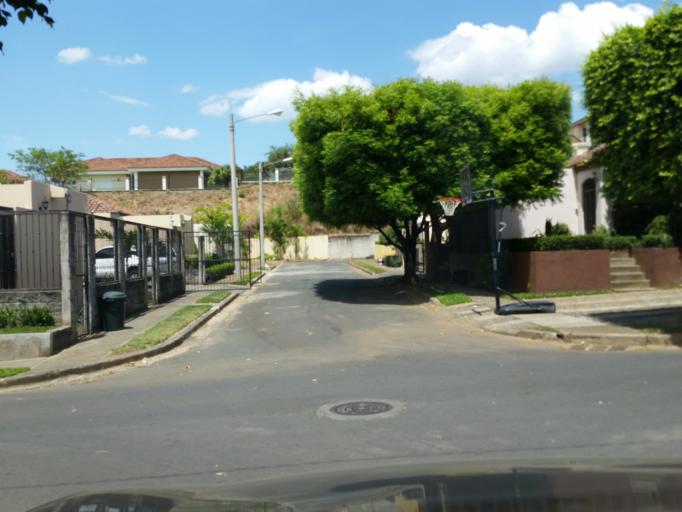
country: NI
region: Managua
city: Managua
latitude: 12.0982
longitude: -86.2553
